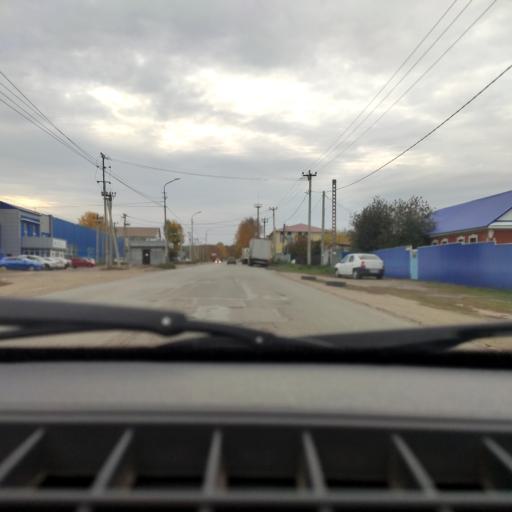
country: RU
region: Bashkortostan
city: Avdon
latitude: 54.6889
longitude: 55.8038
